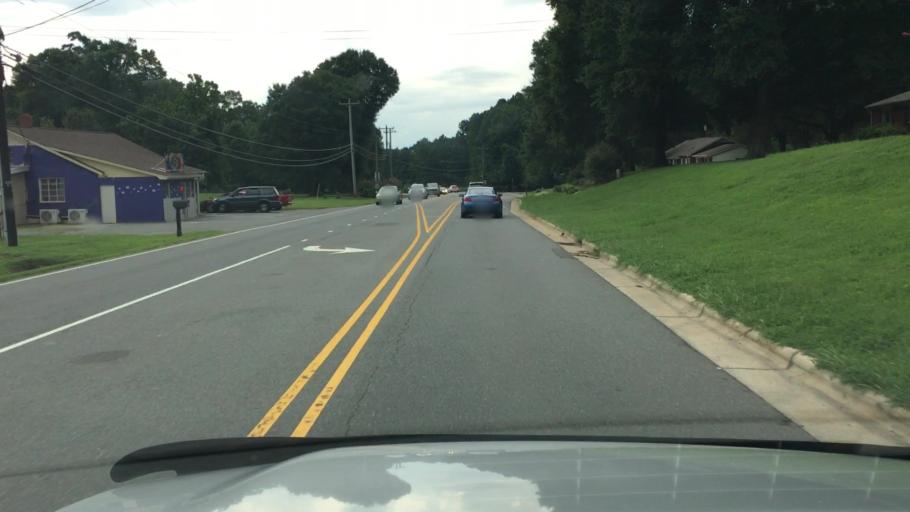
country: US
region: North Carolina
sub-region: Mecklenburg County
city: Huntersville
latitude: 35.3501
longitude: -80.8882
